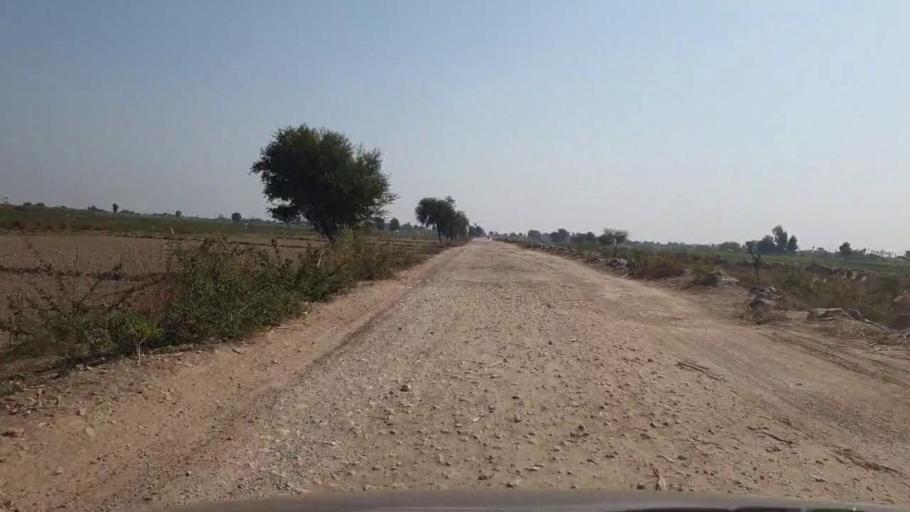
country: PK
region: Sindh
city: Samaro
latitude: 25.2577
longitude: 69.2551
